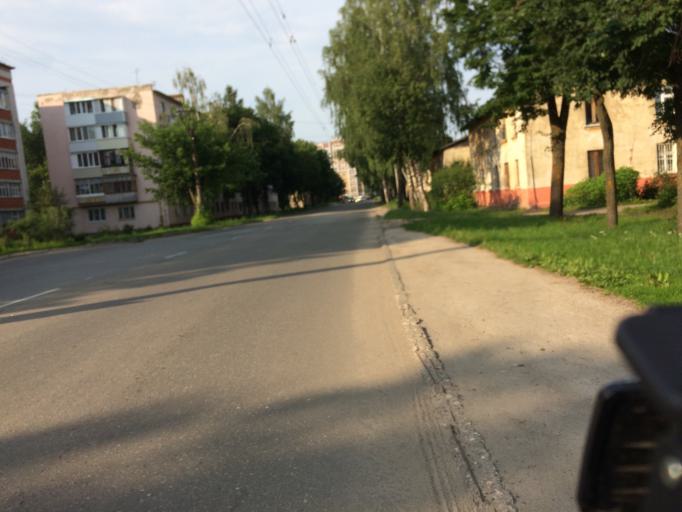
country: RU
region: Mariy-El
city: Yoshkar-Ola
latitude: 56.6295
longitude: 47.9475
